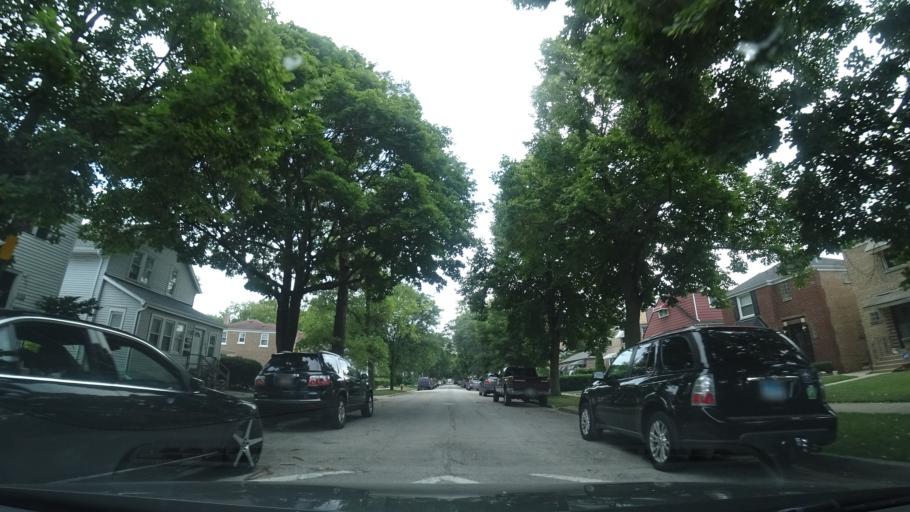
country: US
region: Illinois
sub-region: Cook County
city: Evanston
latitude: 42.0515
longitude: -87.7034
